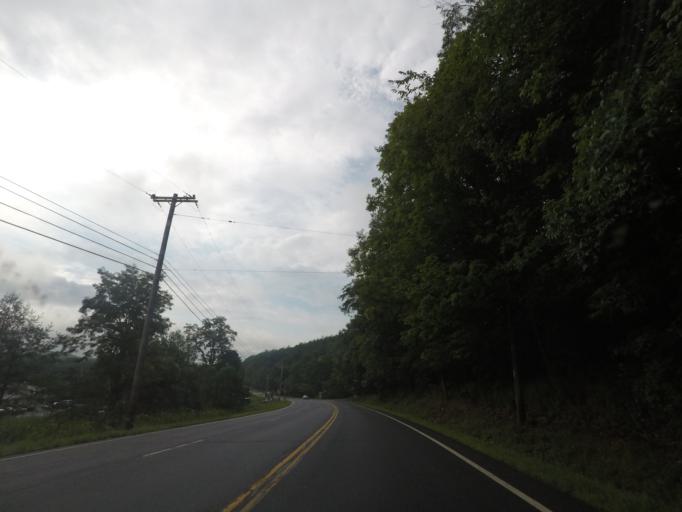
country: US
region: New York
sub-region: Rensselaer County
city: Nassau
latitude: 42.5125
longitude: -73.5695
